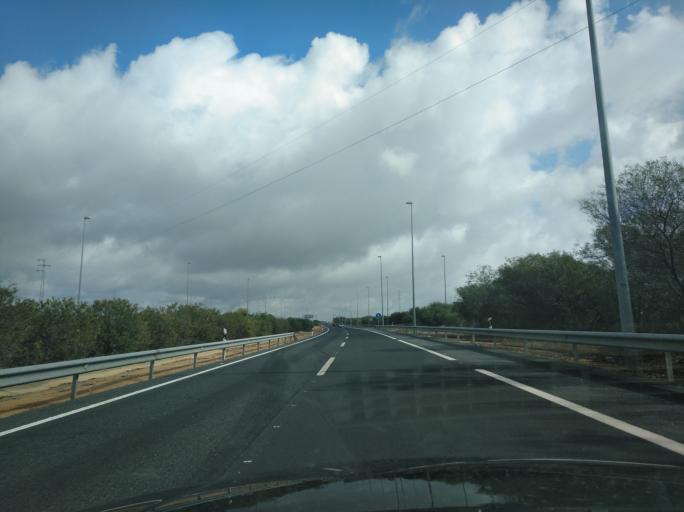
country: ES
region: Andalusia
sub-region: Provincia de Huelva
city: Lepe
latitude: 37.2974
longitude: -7.2184
